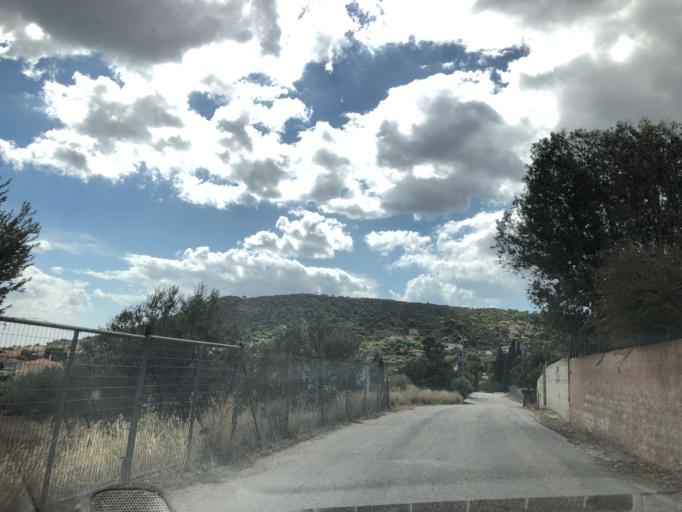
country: GR
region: Attica
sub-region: Nomarchia Anatolikis Attikis
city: Agios Dimitrios Kropias
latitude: 37.8165
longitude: 23.8685
